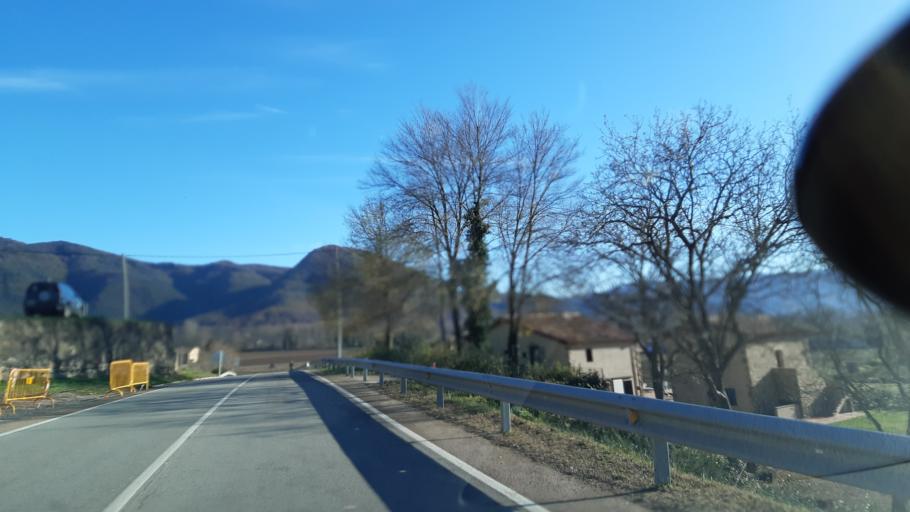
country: ES
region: Catalonia
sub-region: Provincia de Girona
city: Bas
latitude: 42.1475
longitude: 2.4382
